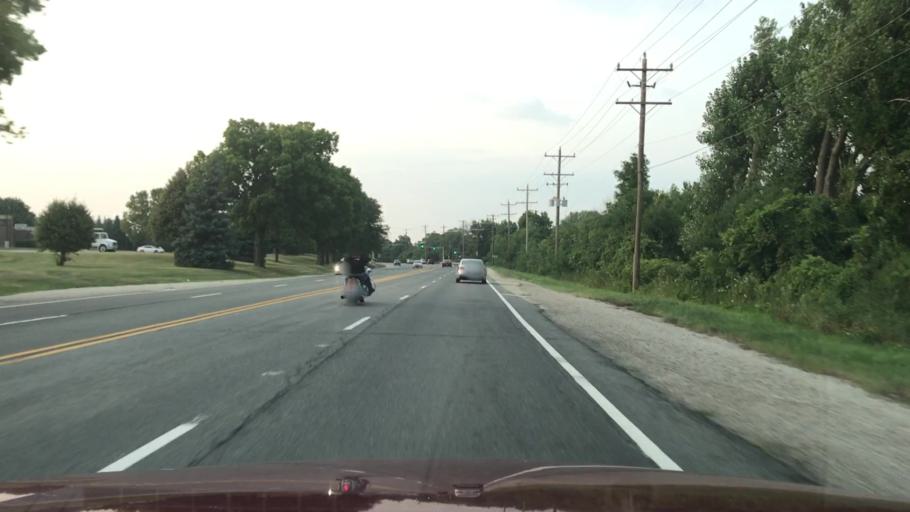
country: US
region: Illinois
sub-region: Will County
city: Lockport
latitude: 41.6084
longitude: -88.0752
